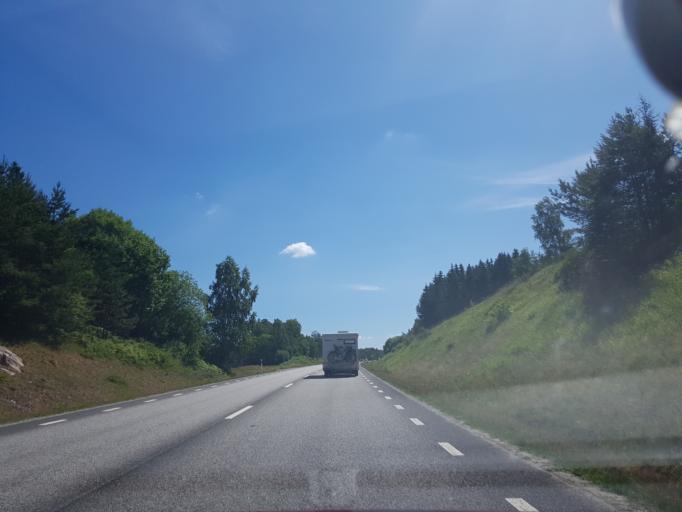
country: SE
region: Vaestra Goetaland
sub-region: Tjorns Kommun
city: Myggenas
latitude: 58.1309
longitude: 11.6732
